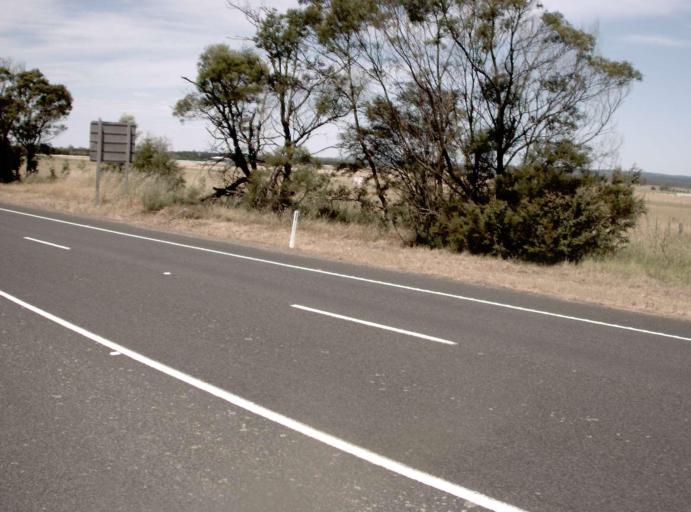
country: AU
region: Victoria
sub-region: Wellington
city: Heyfield
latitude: -38.1188
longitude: 146.8617
